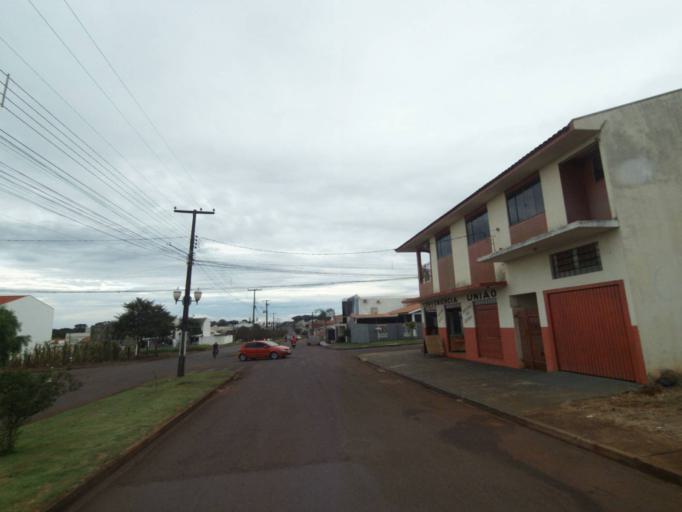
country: BR
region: Parana
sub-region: Campo Mourao
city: Campo Mourao
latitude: -24.0284
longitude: -52.3581
